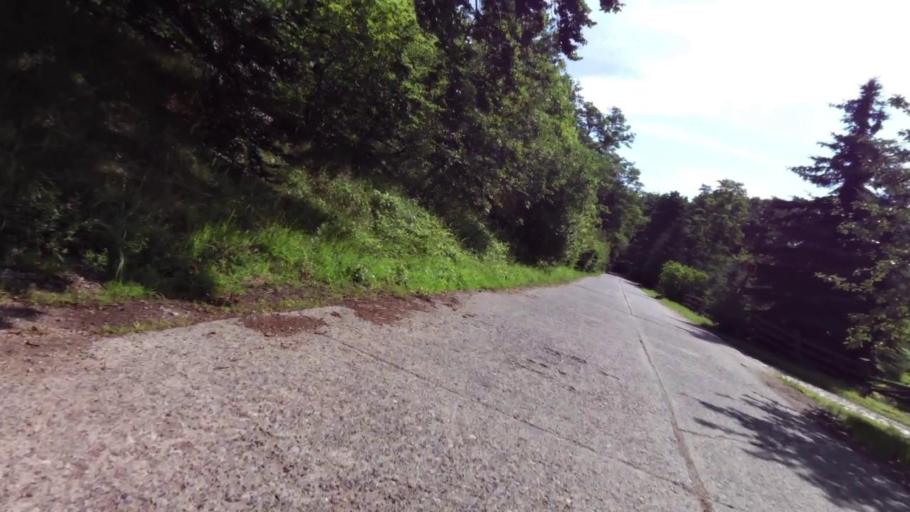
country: PL
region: West Pomeranian Voivodeship
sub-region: Powiat stargardzki
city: Dobrzany
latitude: 53.3891
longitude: 15.4913
